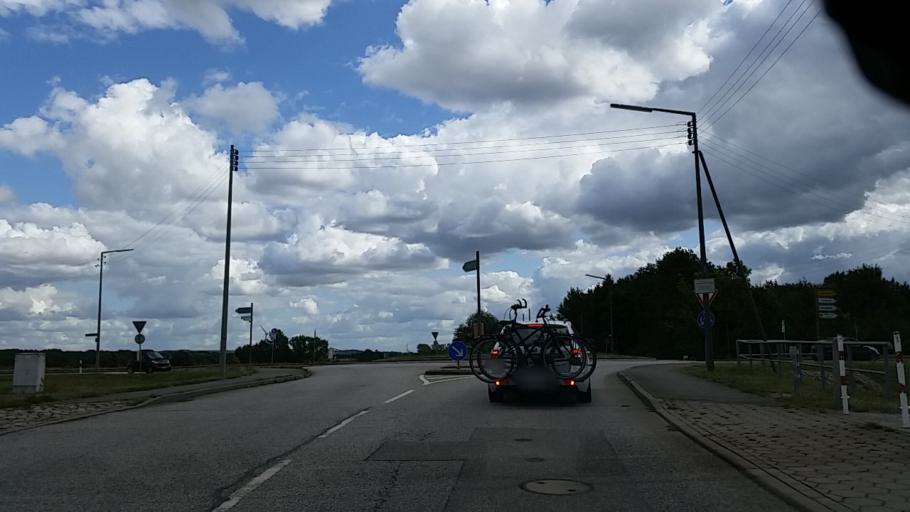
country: DE
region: Schleswig-Holstein
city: Escheburg
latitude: 53.4411
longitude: 10.3031
